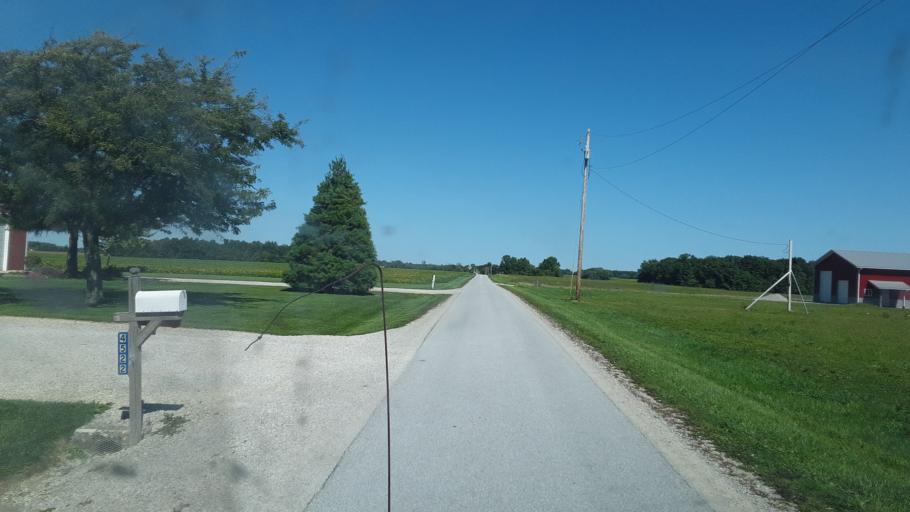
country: US
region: Ohio
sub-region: Sandusky County
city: Mount Carmel
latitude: 41.1901
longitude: -82.8991
